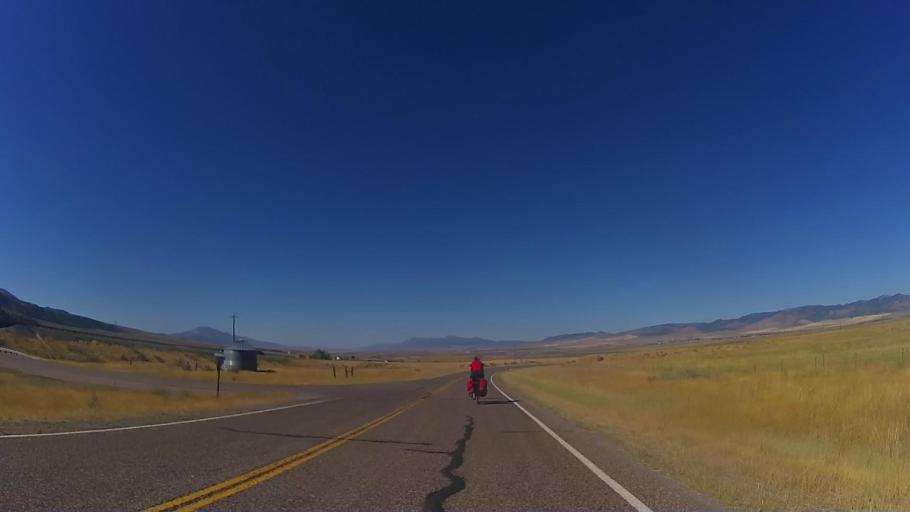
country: US
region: Idaho
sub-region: Oneida County
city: Malad City
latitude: 42.3738
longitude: -112.2089
